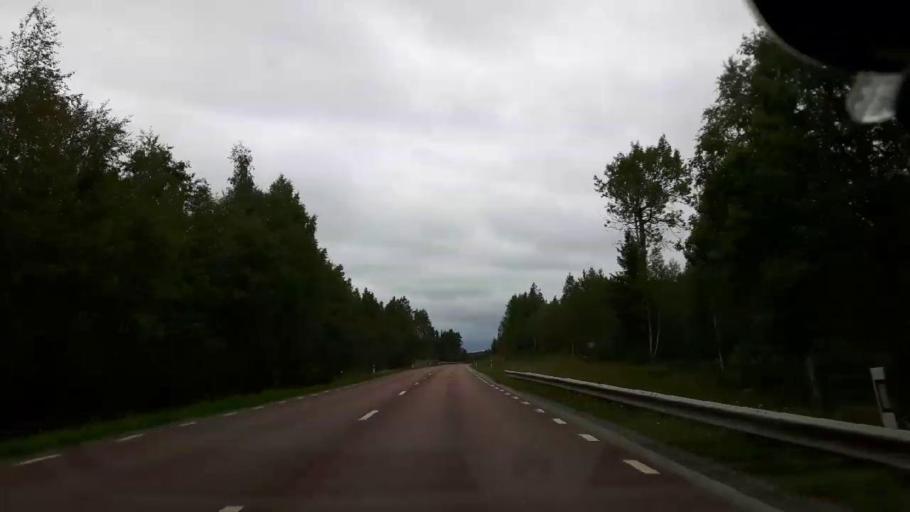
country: SE
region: Jaemtland
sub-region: Bergs Kommun
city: Hoverberg
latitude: 62.8816
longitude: 14.5225
